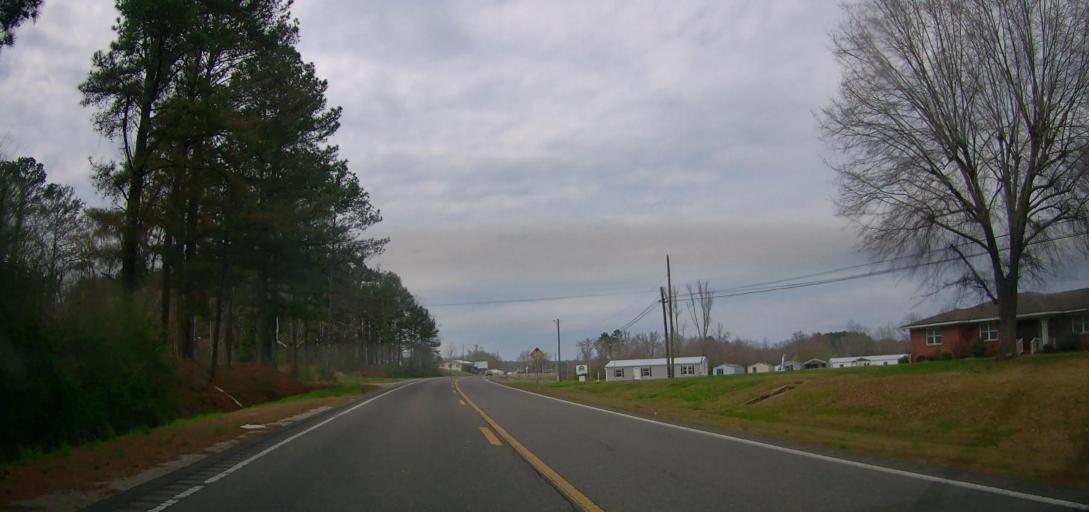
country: US
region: Alabama
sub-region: Marion County
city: Hamilton
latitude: 34.0959
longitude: -87.9871
